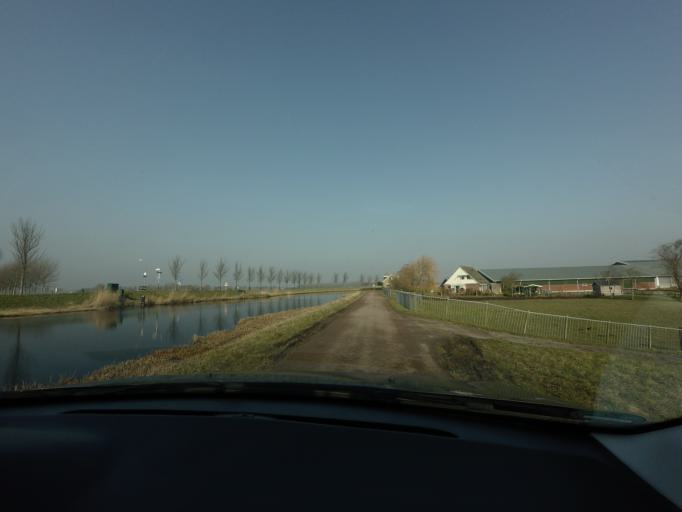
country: NL
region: North Holland
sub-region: Gemeente Beemster
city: Halfweg
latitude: 52.5936
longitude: 4.9497
